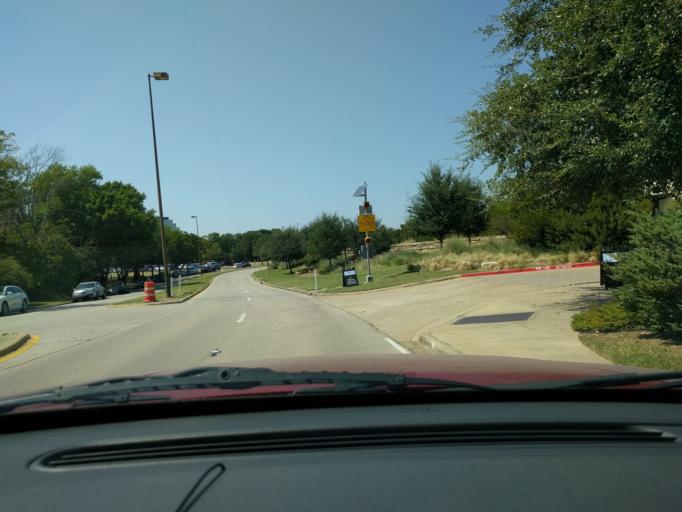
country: US
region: Texas
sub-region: Dallas County
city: Richardson
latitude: 32.9219
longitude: -96.7780
